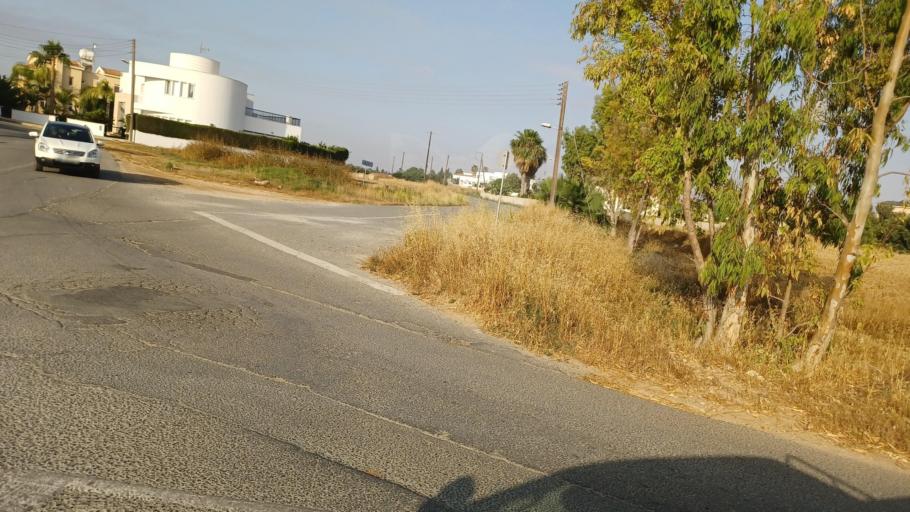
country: CY
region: Ammochostos
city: Paralimni
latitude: 35.0266
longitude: 33.9783
